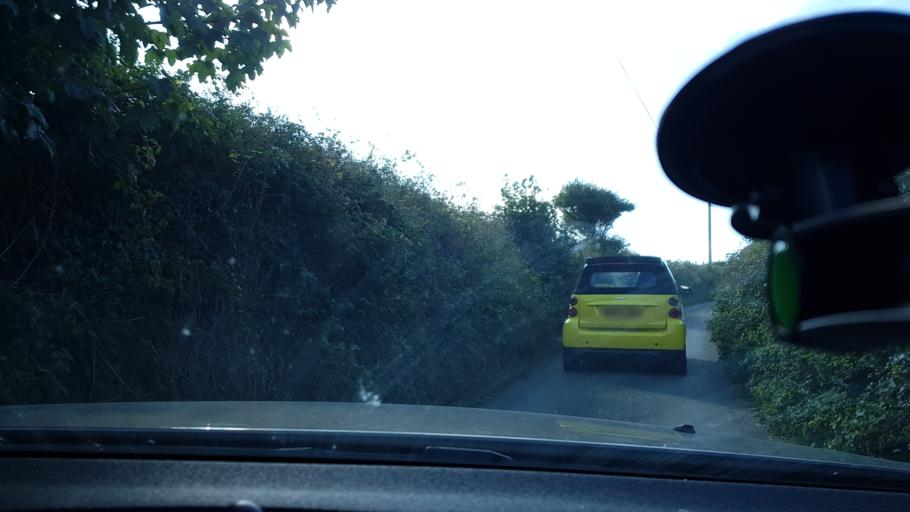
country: GB
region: England
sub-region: Cornwall
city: Tintagel
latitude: 50.6624
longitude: -4.7541
